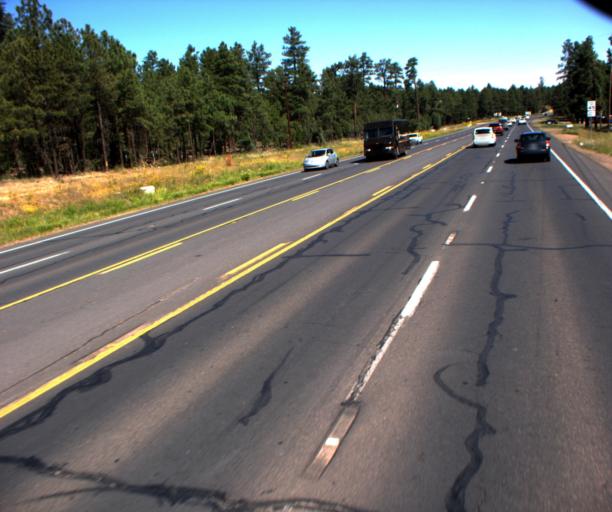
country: US
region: Arizona
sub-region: Navajo County
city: Show Low
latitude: 34.2195
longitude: -110.0290
